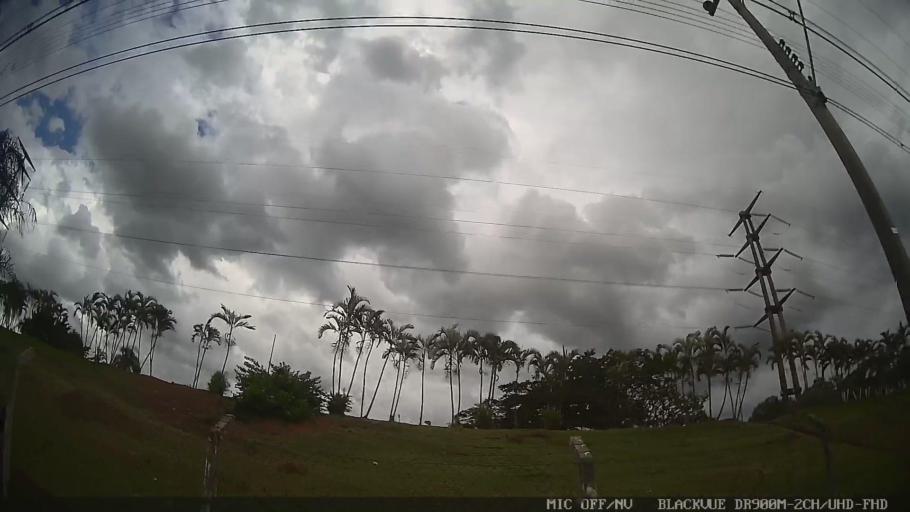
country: BR
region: Sao Paulo
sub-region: Jaguariuna
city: Jaguariuna
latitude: -22.7094
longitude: -47.0054
